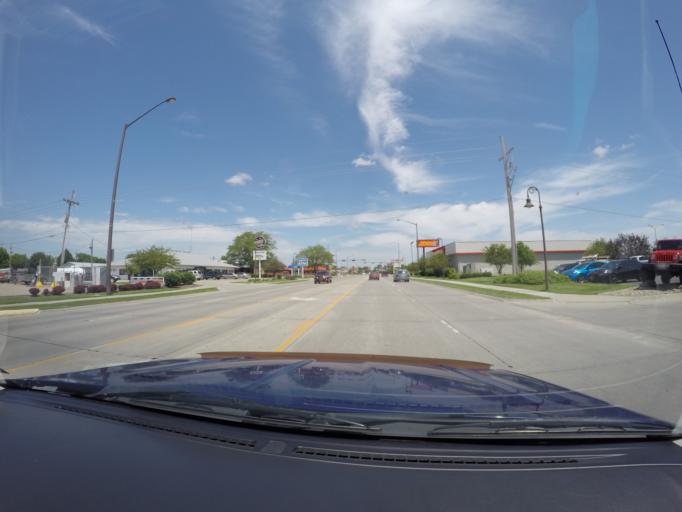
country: US
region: Nebraska
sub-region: Hall County
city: Grand Island
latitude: 40.9041
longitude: -98.3398
